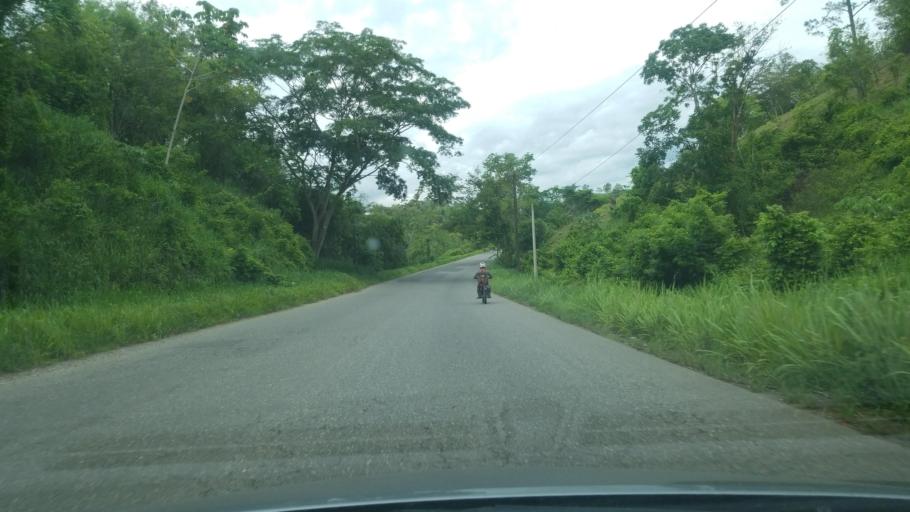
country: HN
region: Santa Barbara
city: La Flecha
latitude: 15.3020
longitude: -88.4549
